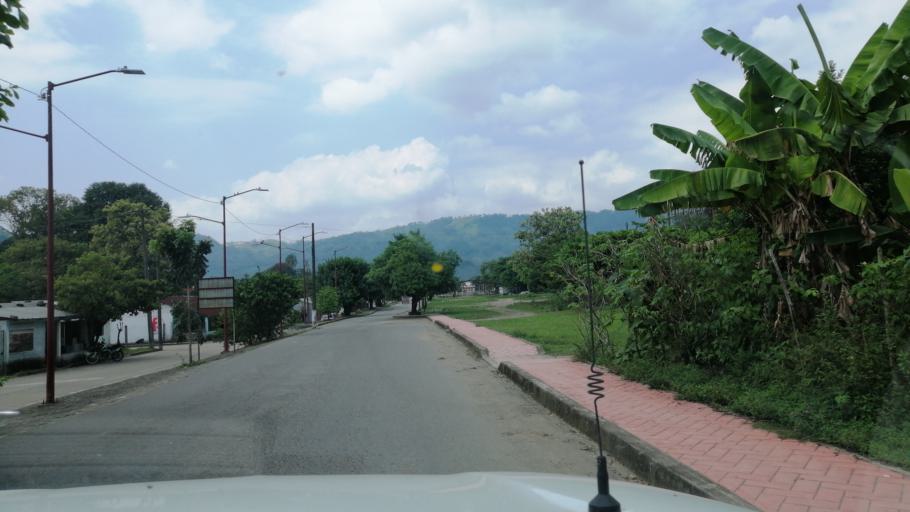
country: MX
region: Chiapas
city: Ostuacan
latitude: 17.4042
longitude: -93.3338
